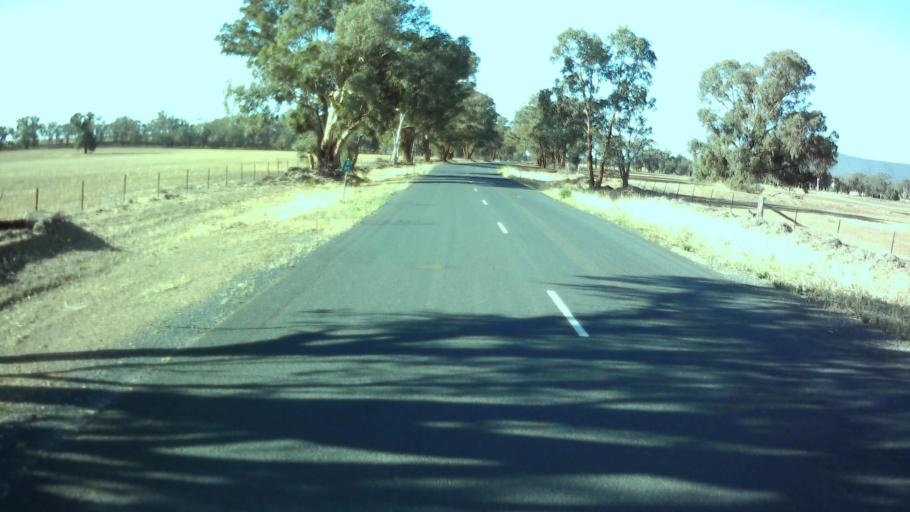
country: AU
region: New South Wales
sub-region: Weddin
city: Grenfell
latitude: -33.9376
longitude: 148.1373
